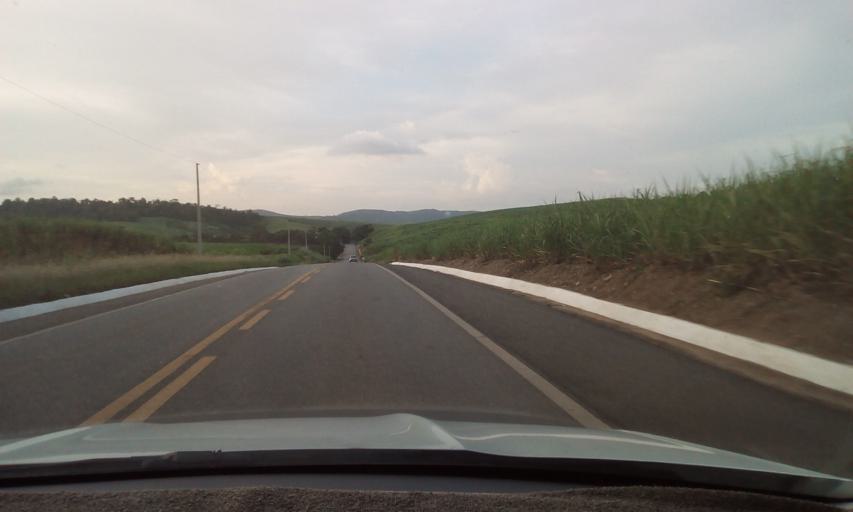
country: BR
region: Pernambuco
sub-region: Vicencia
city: Vicencia
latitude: -7.6501
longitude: -35.2519
